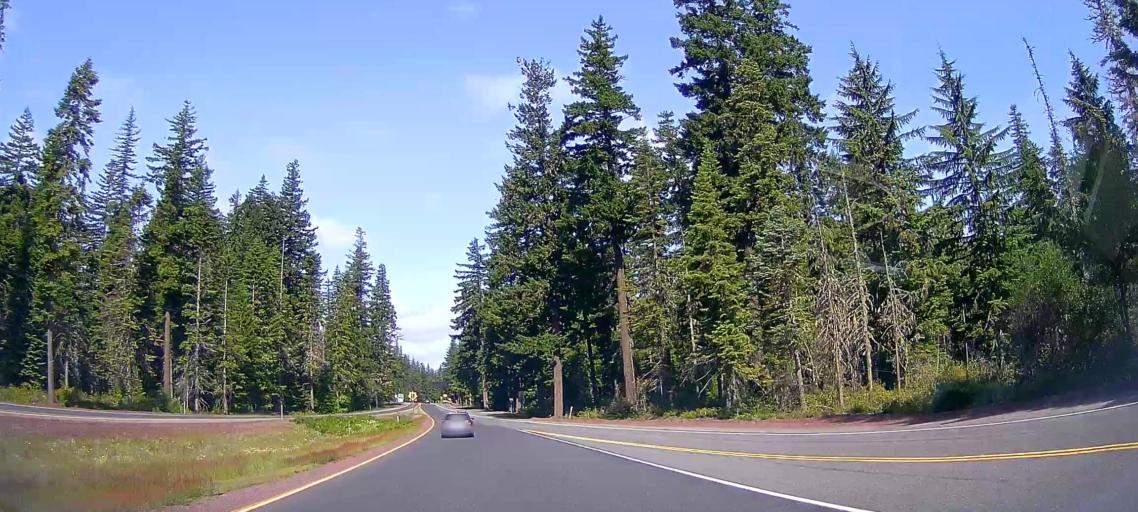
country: US
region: Oregon
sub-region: Clackamas County
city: Mount Hood Village
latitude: 45.1315
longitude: -121.6025
